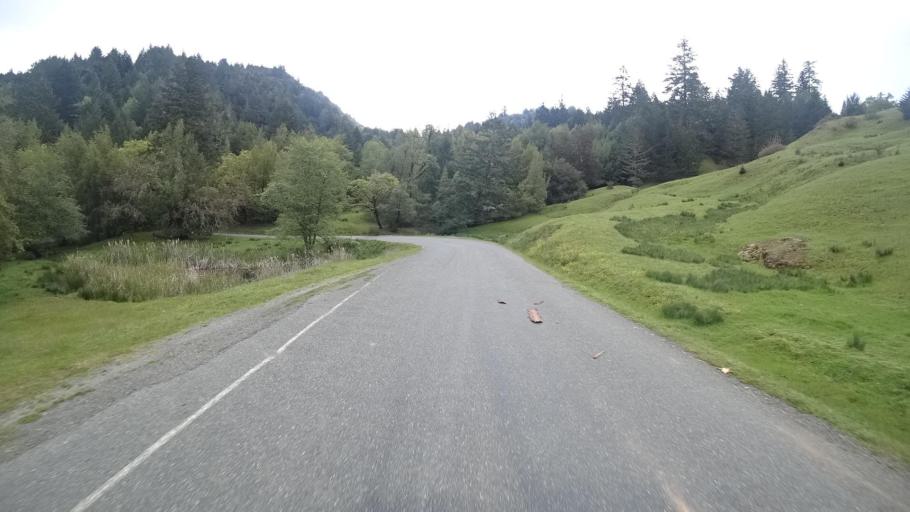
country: US
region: California
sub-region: Humboldt County
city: Redway
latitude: 40.1618
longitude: -123.5621
